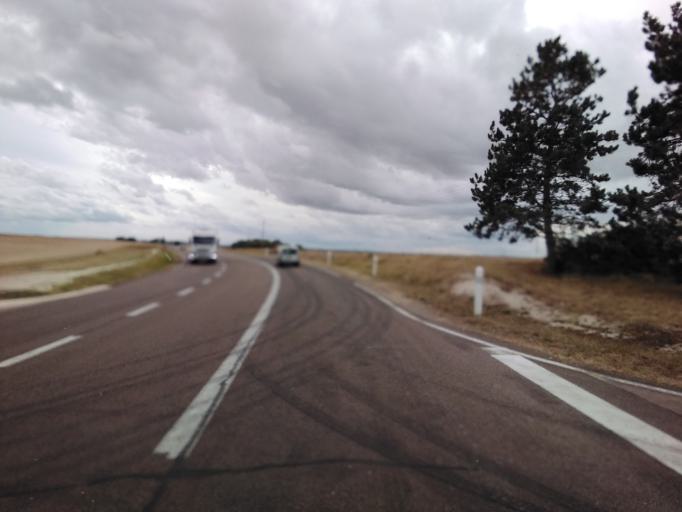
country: FR
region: Champagne-Ardenne
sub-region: Departement de la Marne
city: Frignicourt
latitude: 48.6096
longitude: 4.5554
